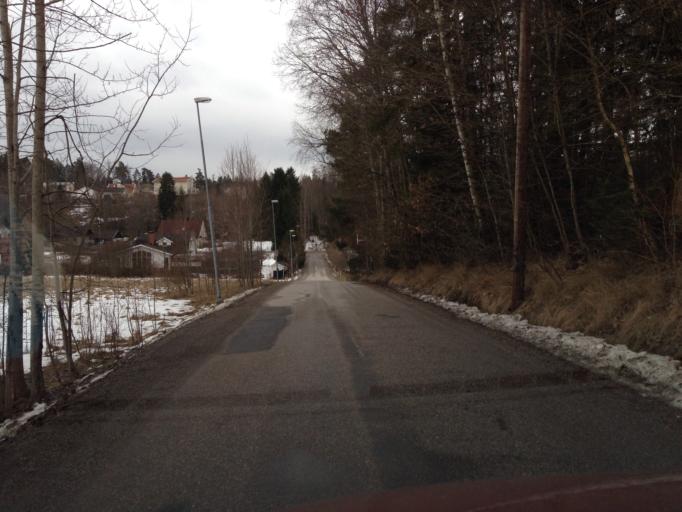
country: SE
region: Stockholm
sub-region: Salems Kommun
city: Ronninge
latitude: 59.1974
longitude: 17.7274
